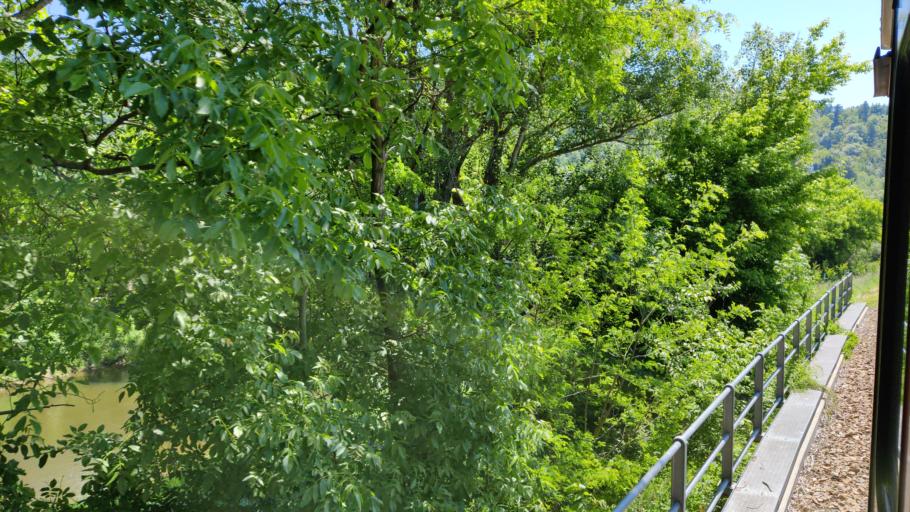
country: AT
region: Lower Austria
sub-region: Politischer Bezirk Krems
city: Langenlois
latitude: 48.5181
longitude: 15.6954
